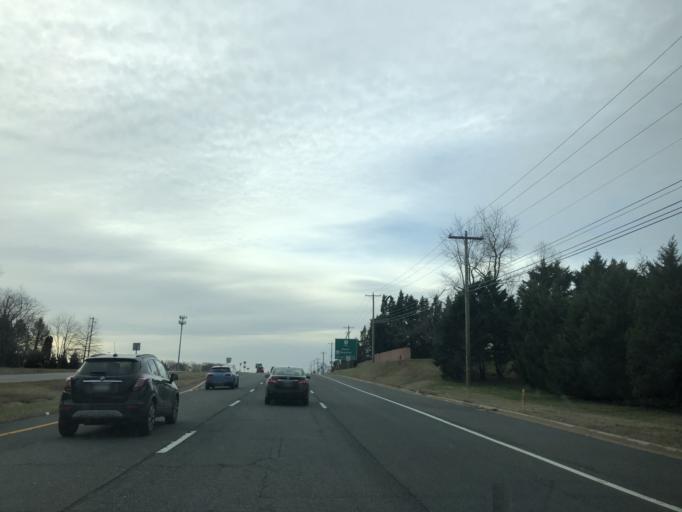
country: US
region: Delaware
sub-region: New Castle County
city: Middletown
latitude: 39.5046
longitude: -75.6495
